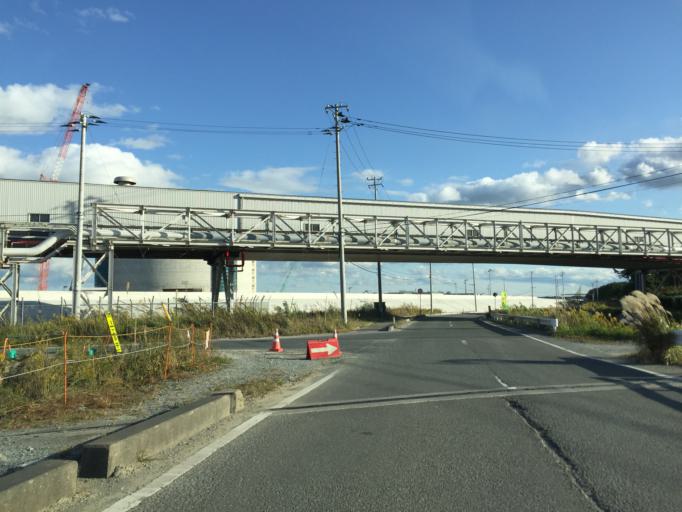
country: JP
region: Miyagi
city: Marumori
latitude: 37.8521
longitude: 140.9464
